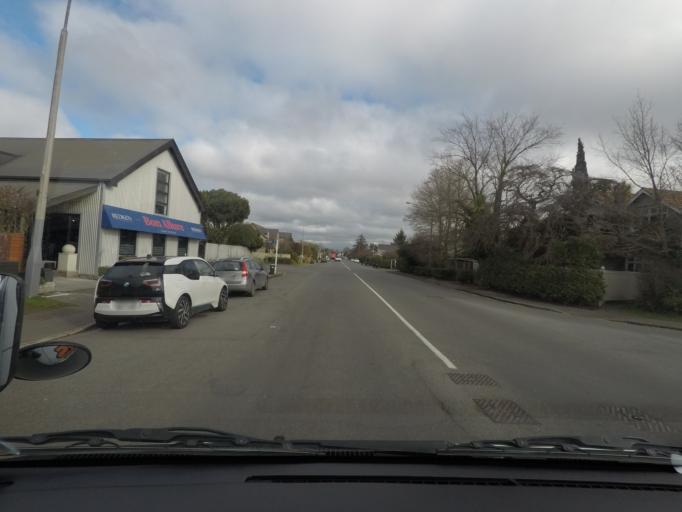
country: NZ
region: Canterbury
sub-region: Christchurch City
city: Christchurch
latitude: -43.5098
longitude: 172.6293
